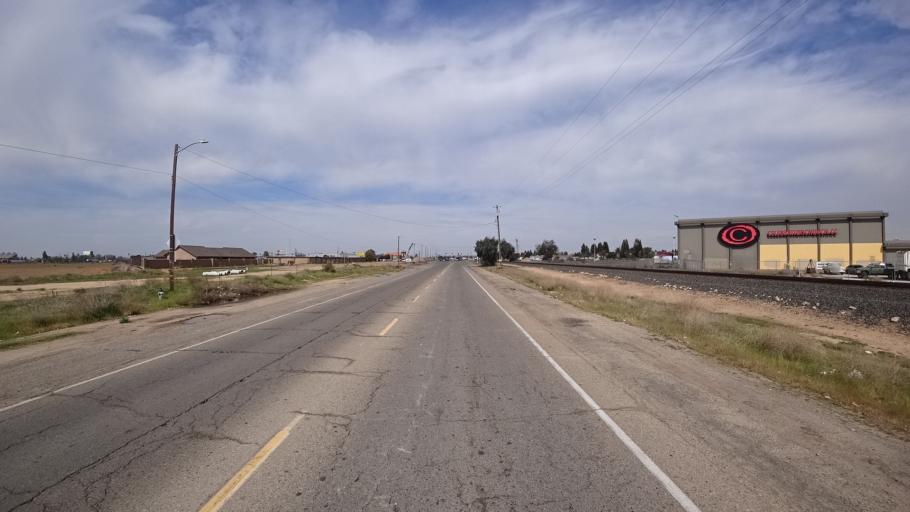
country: US
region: California
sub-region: Fresno County
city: West Park
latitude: 36.8058
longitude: -119.8748
